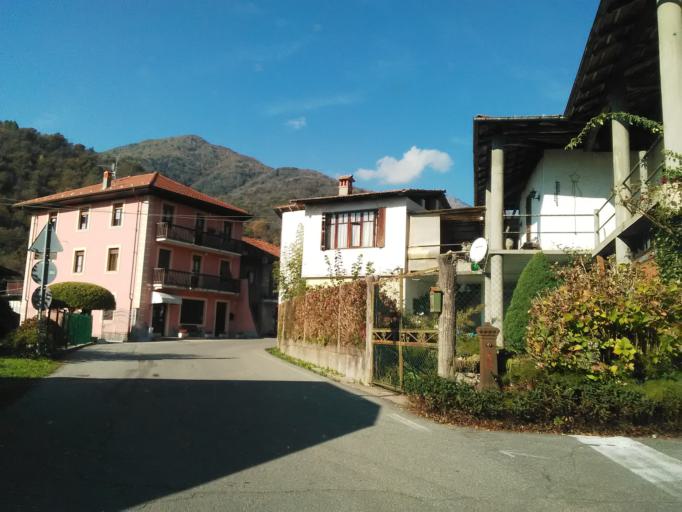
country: IT
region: Piedmont
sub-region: Provincia di Vercelli
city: Postua
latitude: 45.7154
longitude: 8.2278
